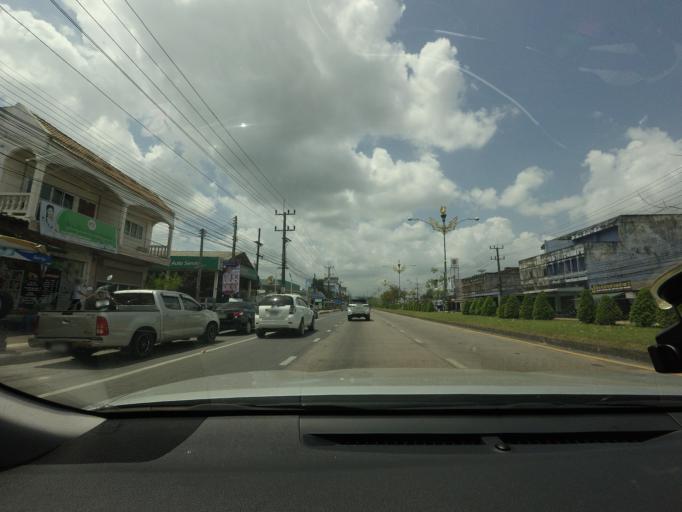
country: TH
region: Nakhon Si Thammarat
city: Nakhon Si Thammarat
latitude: 8.4340
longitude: 99.9255
